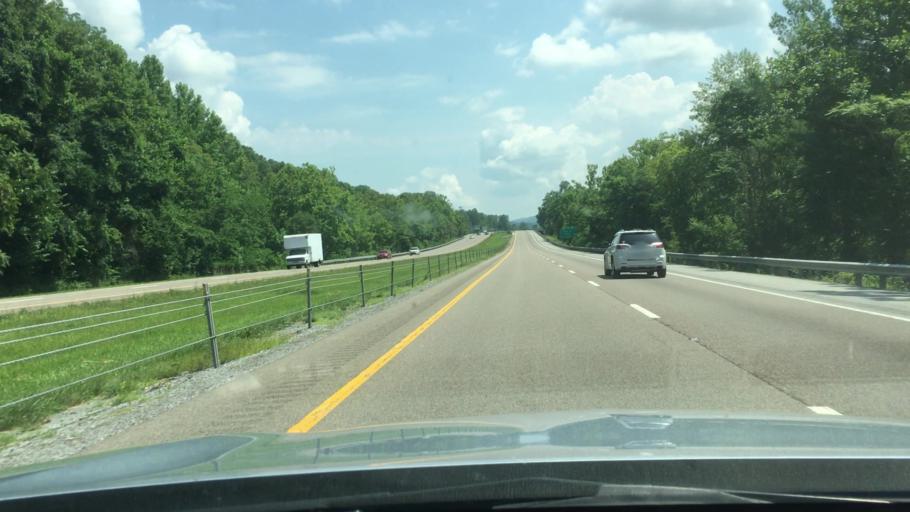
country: US
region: Tennessee
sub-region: Unicoi County
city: Erwin
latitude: 36.1570
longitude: -82.4106
